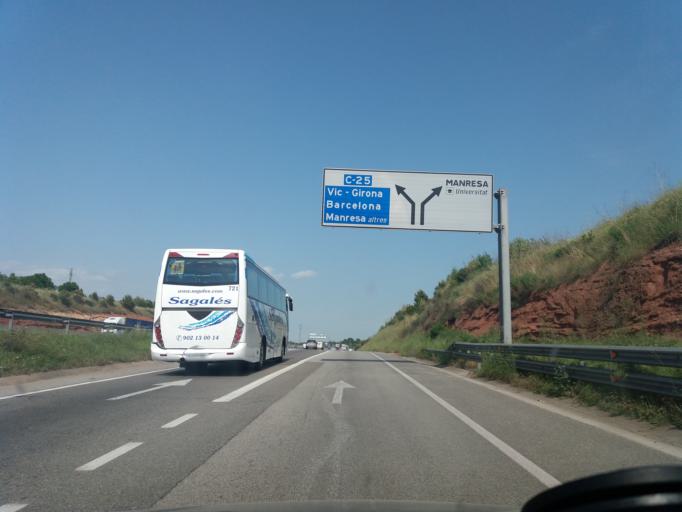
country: ES
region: Catalonia
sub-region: Provincia de Barcelona
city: Sant Joan de Vilatorrada
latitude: 41.7391
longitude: 1.8119
